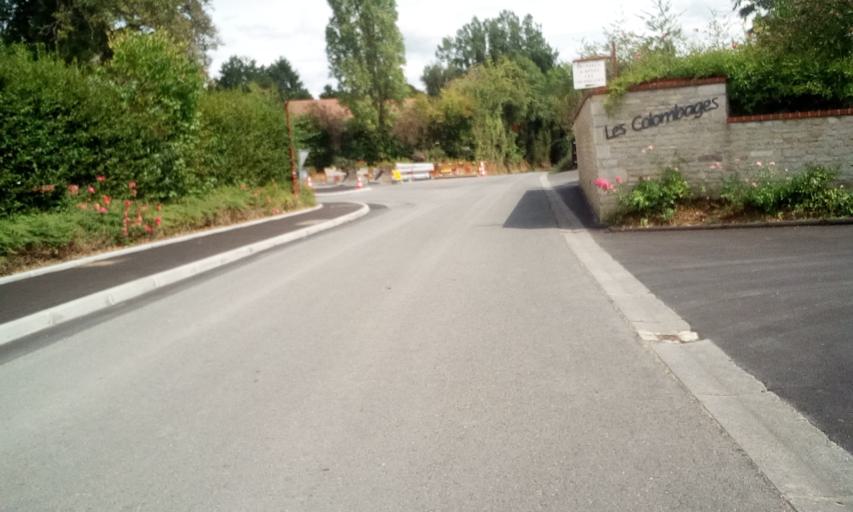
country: FR
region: Lower Normandy
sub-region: Departement du Calvados
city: Bavent
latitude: 49.2418
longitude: -0.1736
